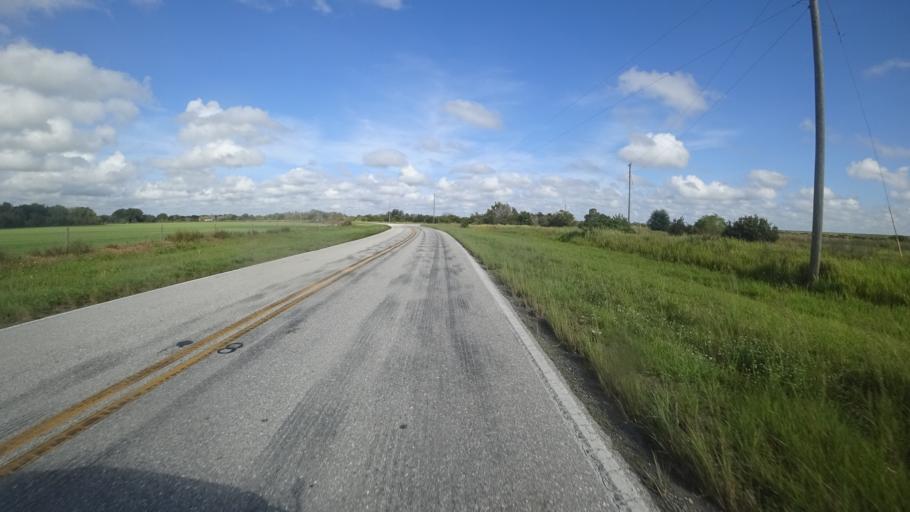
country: US
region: Florida
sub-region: Hardee County
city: Wauchula
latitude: 27.5346
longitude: -82.0785
